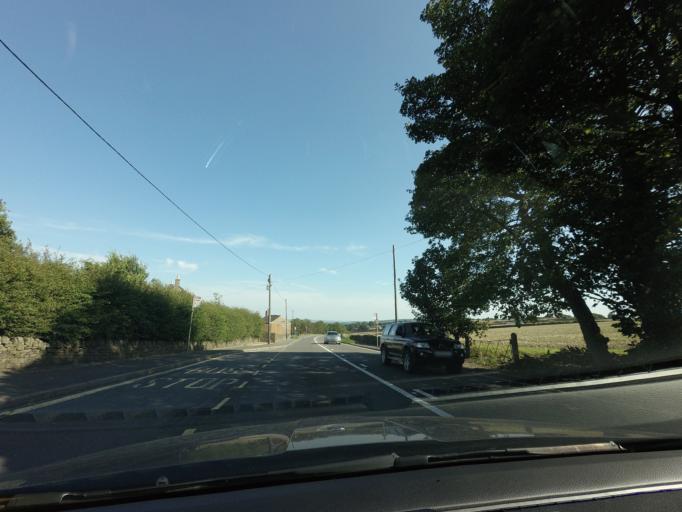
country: GB
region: England
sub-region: Derbyshire
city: Dronfield
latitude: 53.2347
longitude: -1.5327
